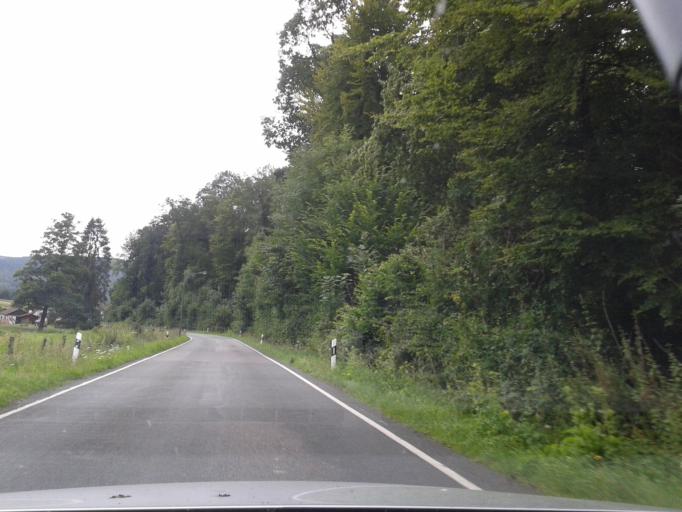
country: DE
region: North Rhine-Westphalia
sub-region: Regierungsbezirk Detmold
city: Blomberg
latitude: 51.9335
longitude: 9.1501
